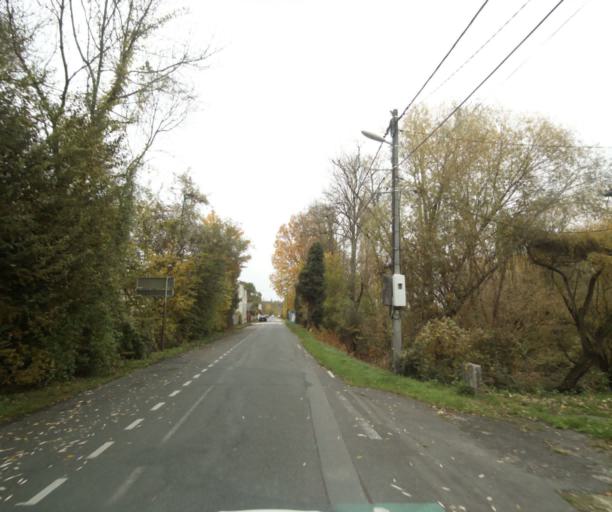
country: FR
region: Poitou-Charentes
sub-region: Departement de la Charente-Maritime
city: Saintes
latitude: 45.7282
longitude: -0.6388
